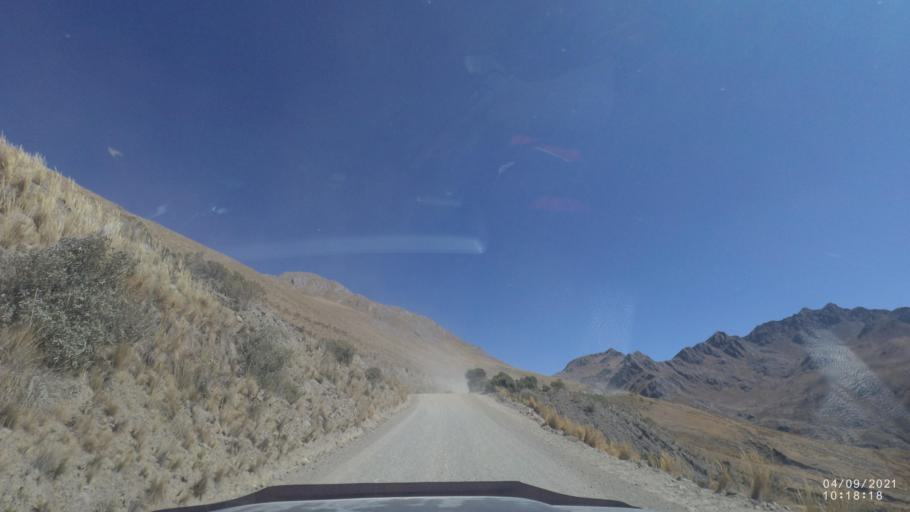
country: BO
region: Cochabamba
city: Sipe Sipe
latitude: -17.3209
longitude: -66.4225
